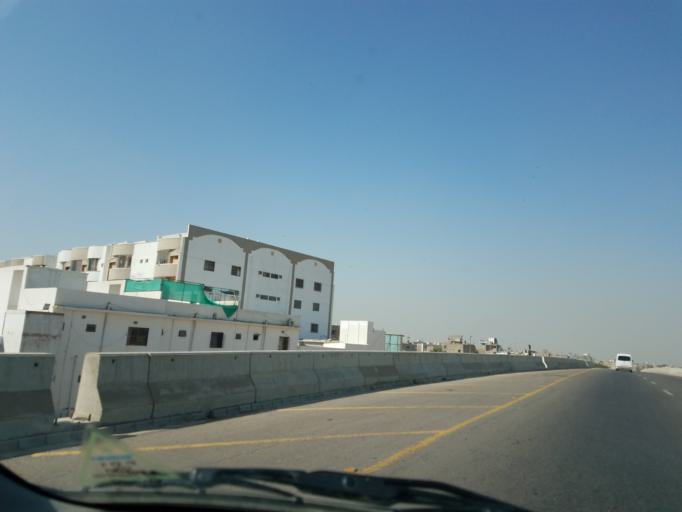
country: PK
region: Sindh
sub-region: Karachi District
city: Karachi
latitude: 24.9159
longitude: 67.0782
